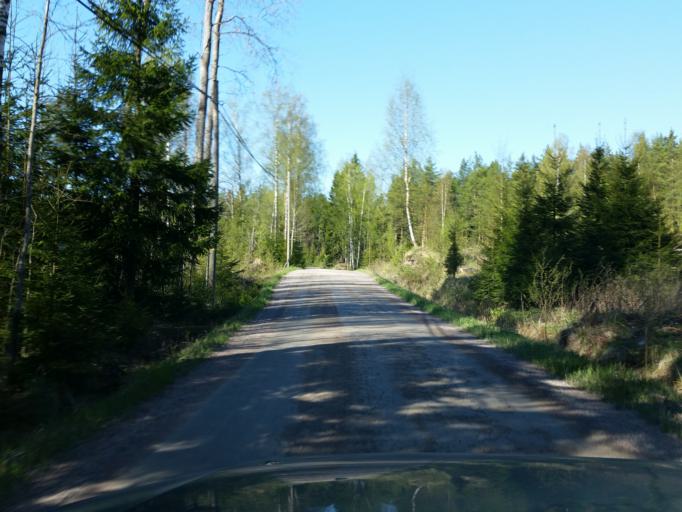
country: FI
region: Uusimaa
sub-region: Helsinki
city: Espoo
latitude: 60.1111
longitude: 24.6196
